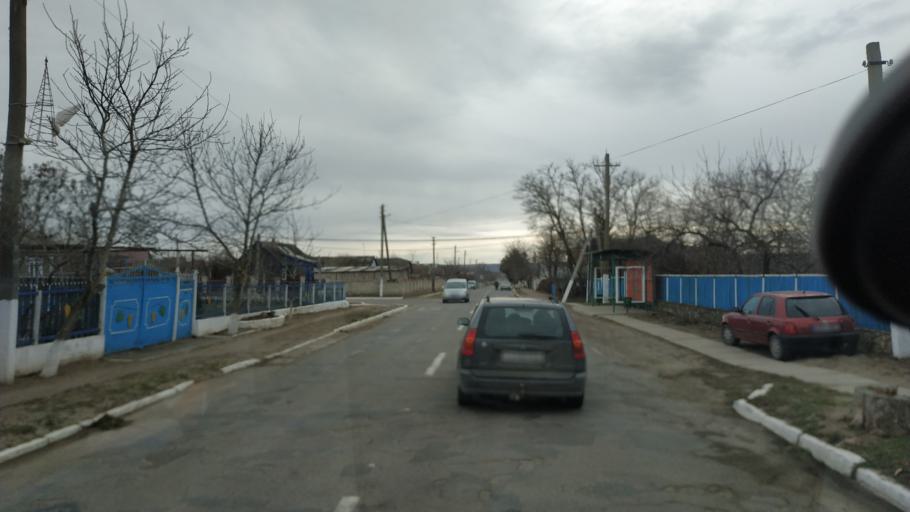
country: MD
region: Telenesti
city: Cocieri
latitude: 47.3028
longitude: 29.1133
